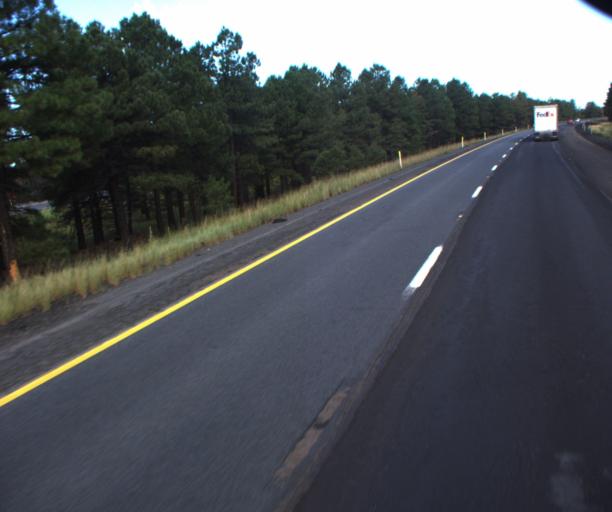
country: US
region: Arizona
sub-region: Coconino County
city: Flagstaff
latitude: 35.2161
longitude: -111.7845
